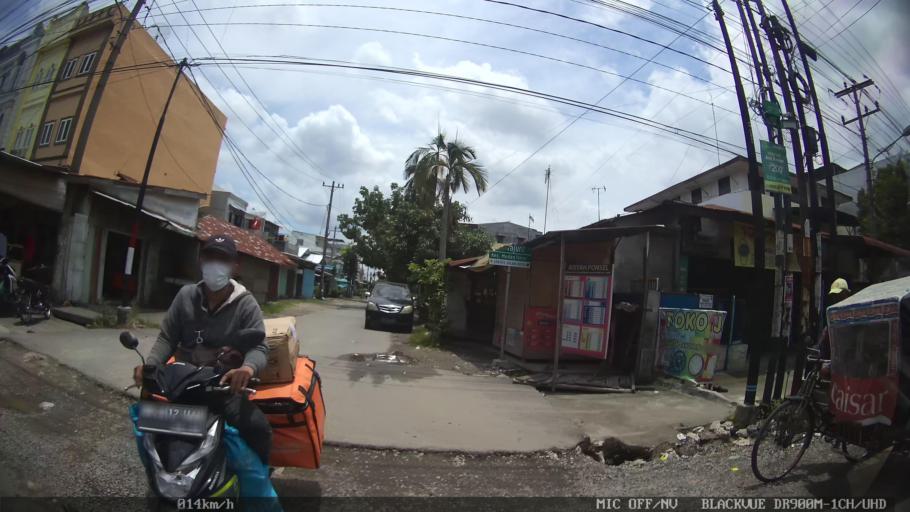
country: ID
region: North Sumatra
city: Medan
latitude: 3.6167
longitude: 98.6837
